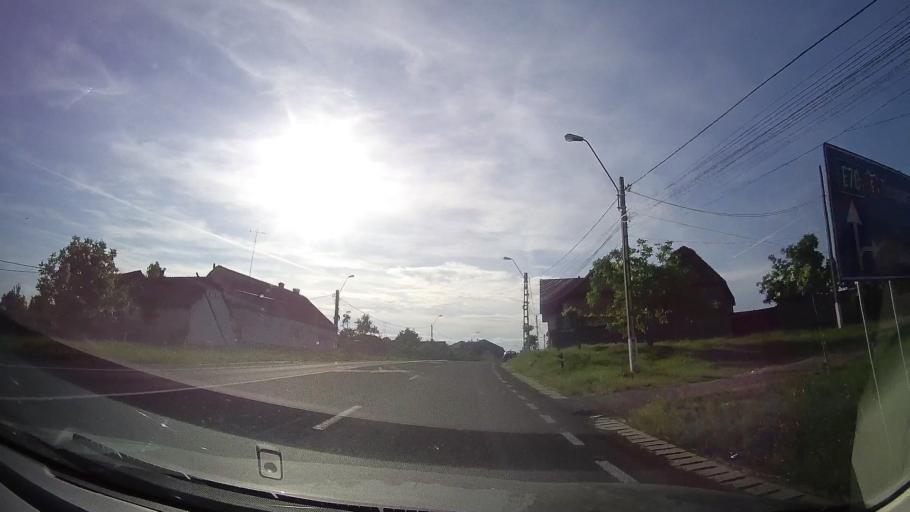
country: RO
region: Timis
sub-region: Oras Recas
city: Recas
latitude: 45.7996
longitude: 21.5148
